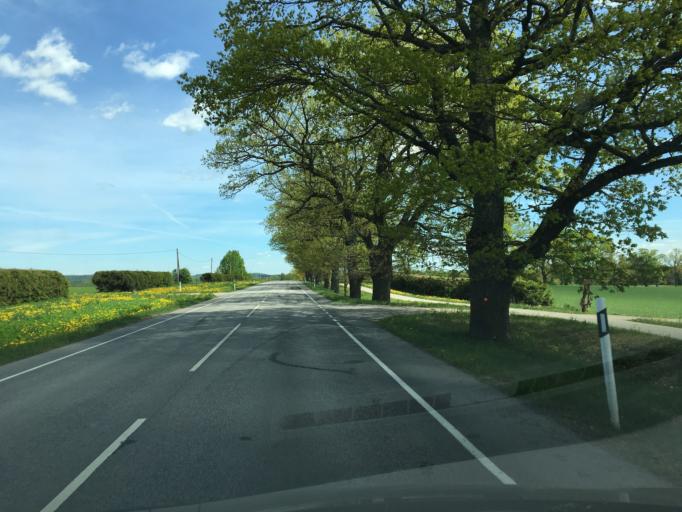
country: EE
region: Vorumaa
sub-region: Antsla vald
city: Vana-Antsla
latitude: 57.9186
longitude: 26.3116
